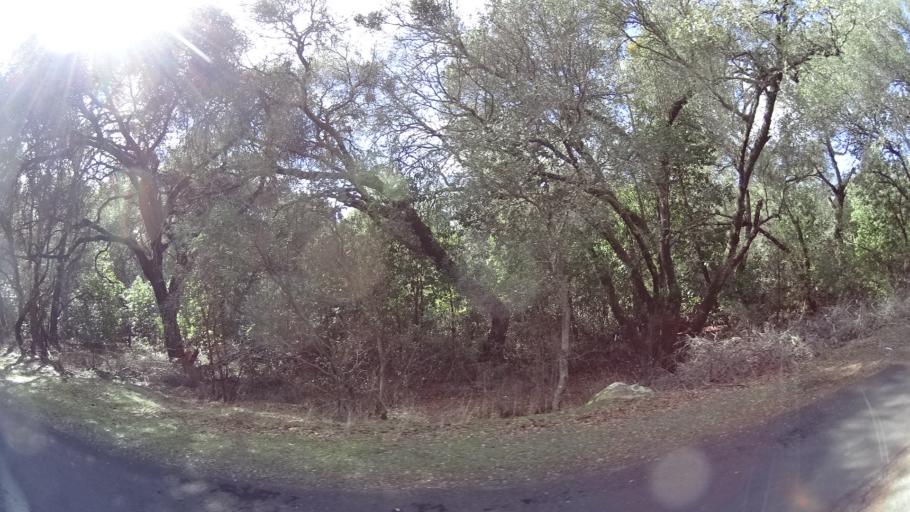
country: US
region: California
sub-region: Butte County
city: Oroville
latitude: 39.5944
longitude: -121.5304
